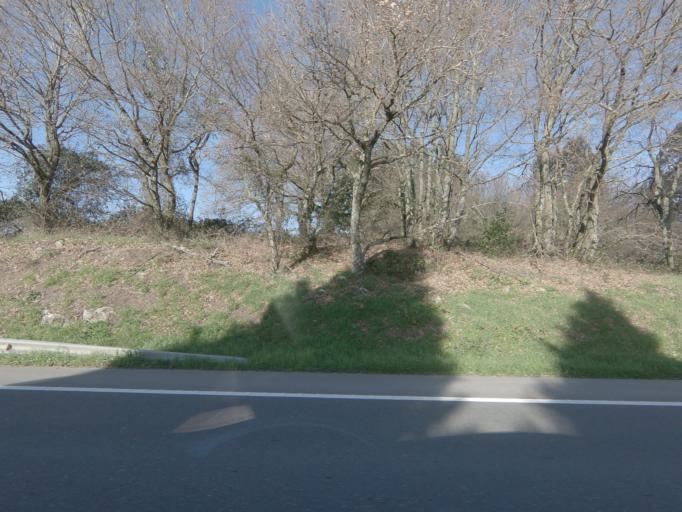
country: ES
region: Galicia
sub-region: Provincia de Pontevedra
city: Silleda
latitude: 42.7082
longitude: -8.2683
